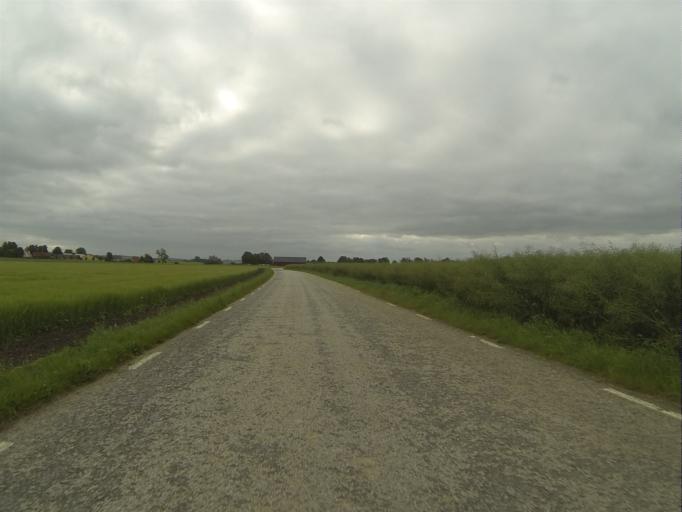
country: SE
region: Skane
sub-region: Staffanstorps Kommun
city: Staffanstorp
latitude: 55.6628
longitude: 13.2525
